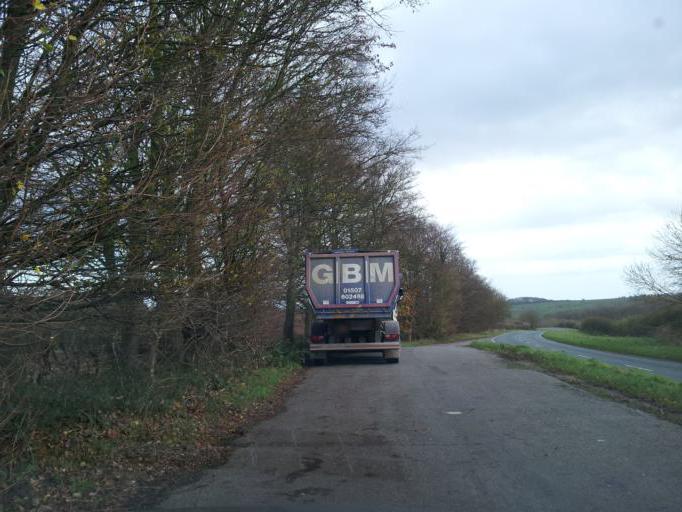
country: GB
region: England
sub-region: Lincolnshire
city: Louth
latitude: 53.3638
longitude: -0.0690
